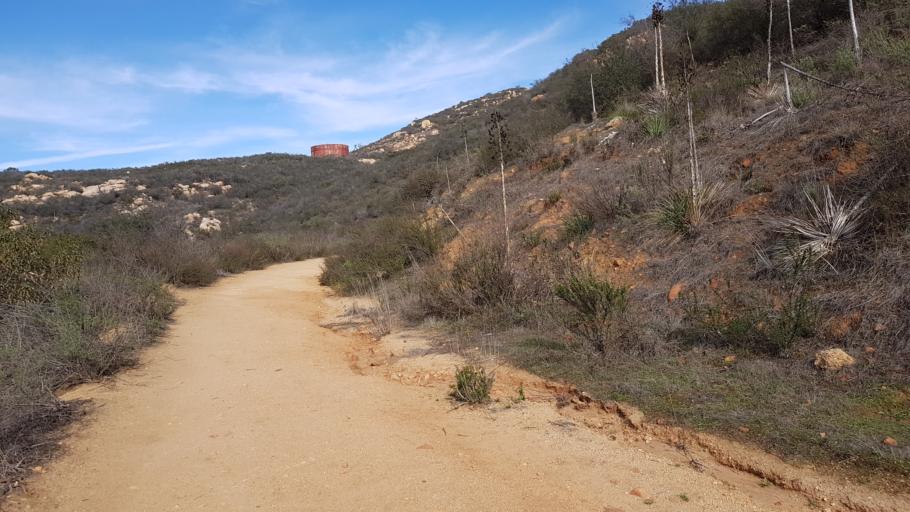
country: US
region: California
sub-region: San Diego County
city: Valley Center
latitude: 33.1751
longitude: -117.0356
